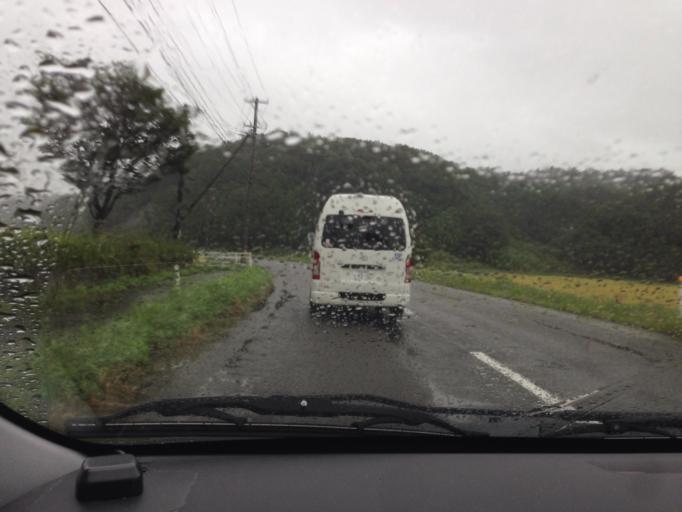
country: JP
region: Fukushima
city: Koriyama
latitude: 37.4189
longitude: 140.2761
